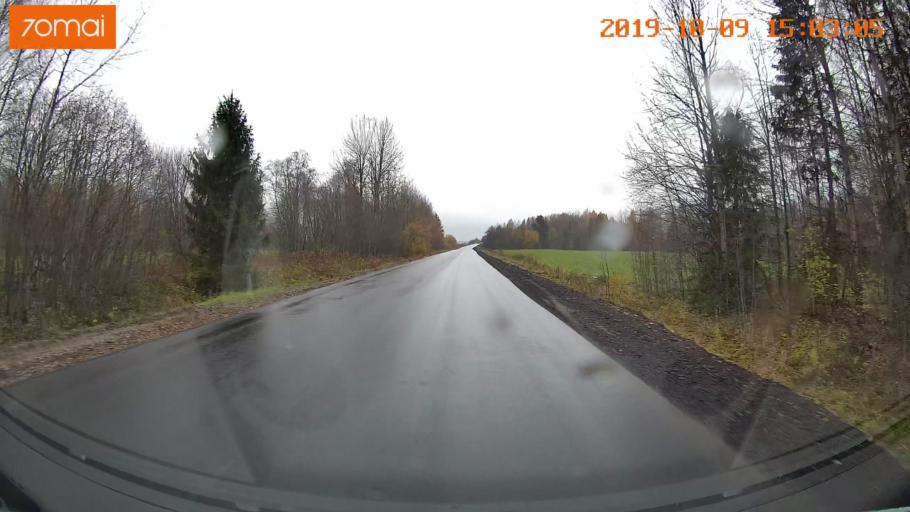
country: RU
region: Kostroma
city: Chistyye Bory
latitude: 58.2763
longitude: 41.6763
